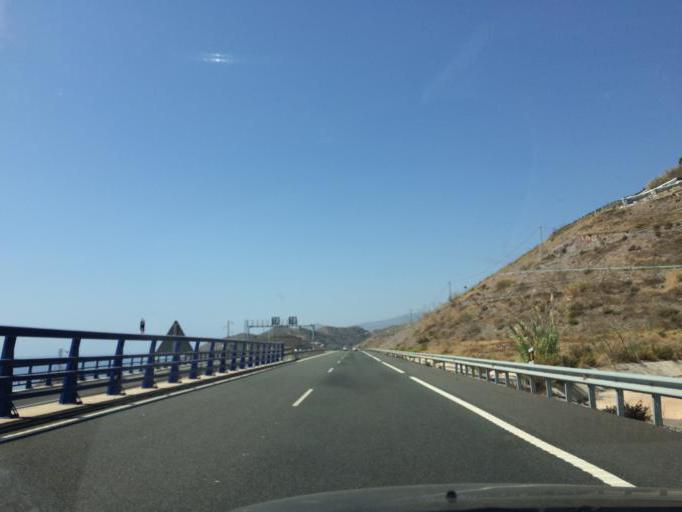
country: ES
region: Andalusia
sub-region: Provincia de Granada
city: Sorvilan
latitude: 36.7551
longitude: -3.2628
